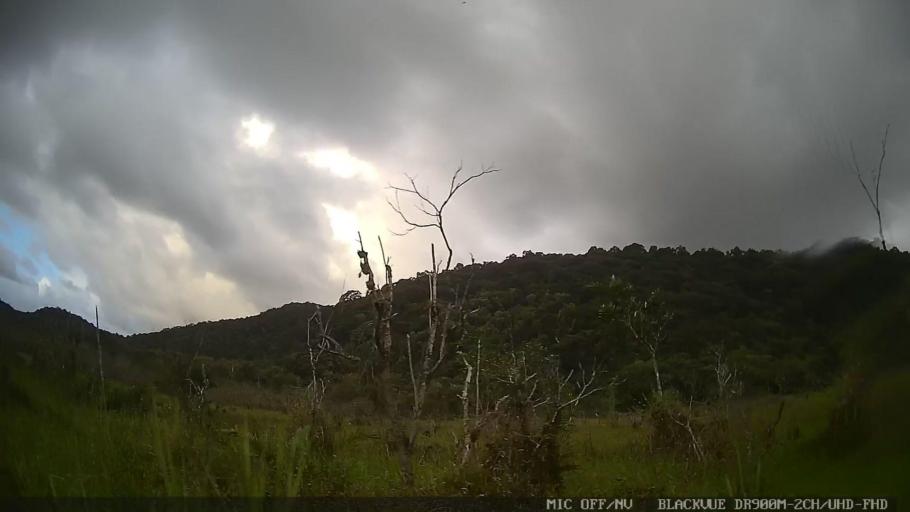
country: BR
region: Sao Paulo
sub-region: Itanhaem
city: Itanhaem
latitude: -24.1398
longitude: -46.7765
